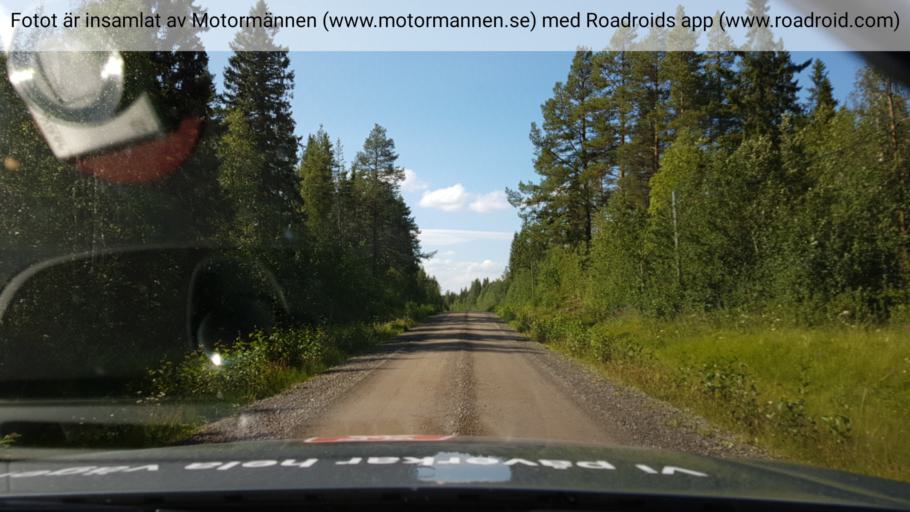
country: SE
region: Vaesterbotten
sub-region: Dorotea Kommun
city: Dorotea
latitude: 64.0941
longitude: 16.4550
